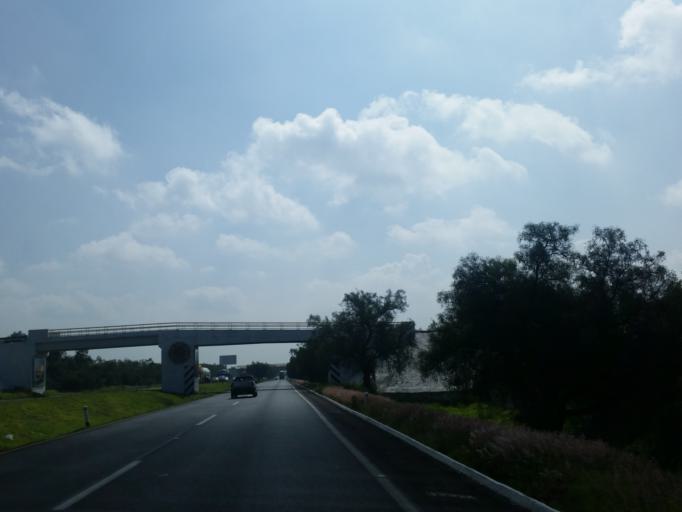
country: MX
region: Mexico
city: Acolman
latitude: 19.6230
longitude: -98.9379
